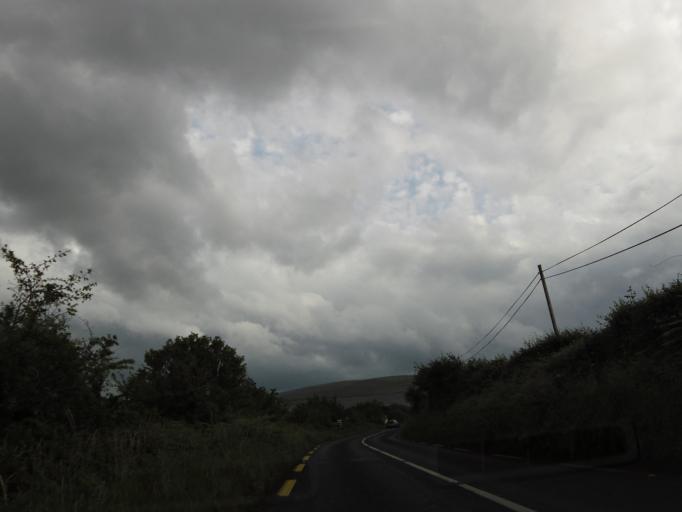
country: IE
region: Connaught
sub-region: County Galway
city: Bearna
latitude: 53.1230
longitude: -9.0749
